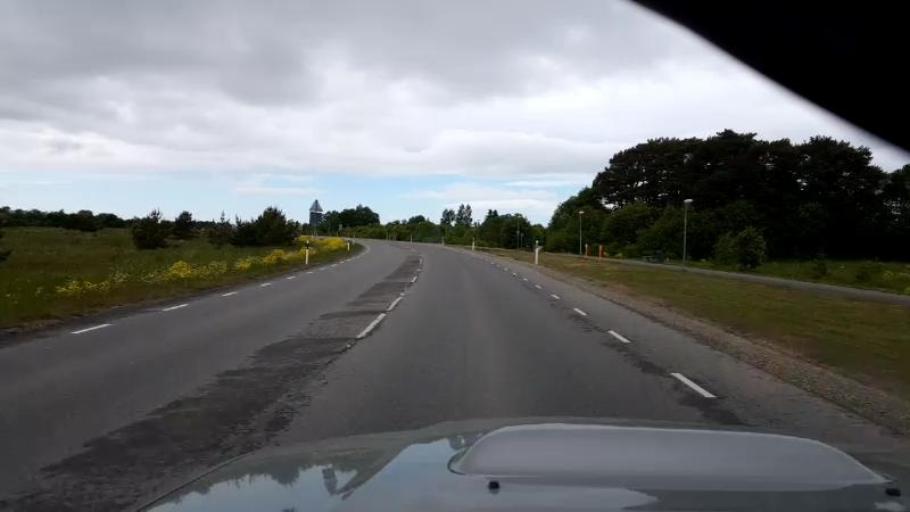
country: EE
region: Harju
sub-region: Harku vald
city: Tabasalu
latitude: 59.4531
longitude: 24.4534
